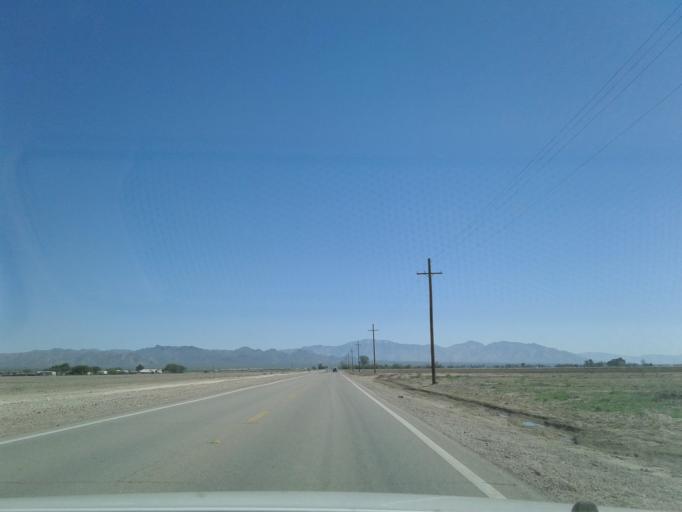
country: US
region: Arizona
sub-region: Pima County
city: Marana
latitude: 32.4604
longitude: -111.2611
